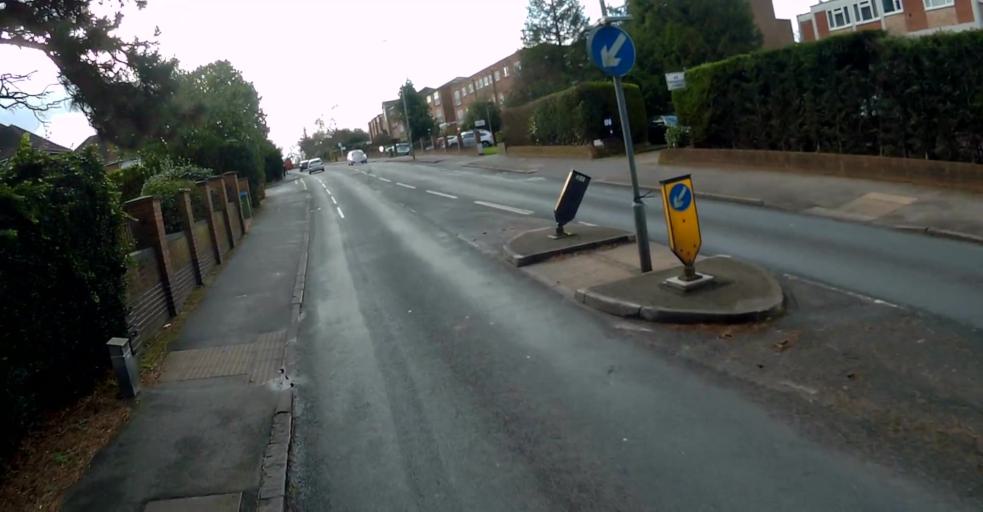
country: GB
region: England
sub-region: Surrey
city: Walton-on-Thames
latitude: 51.3829
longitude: -0.4295
